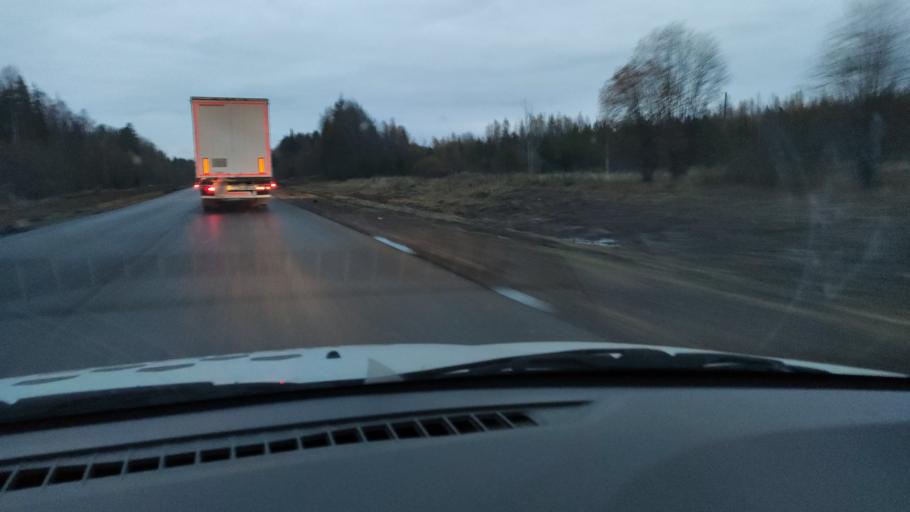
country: RU
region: Kirov
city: Kostino
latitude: 58.8201
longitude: 53.3495
